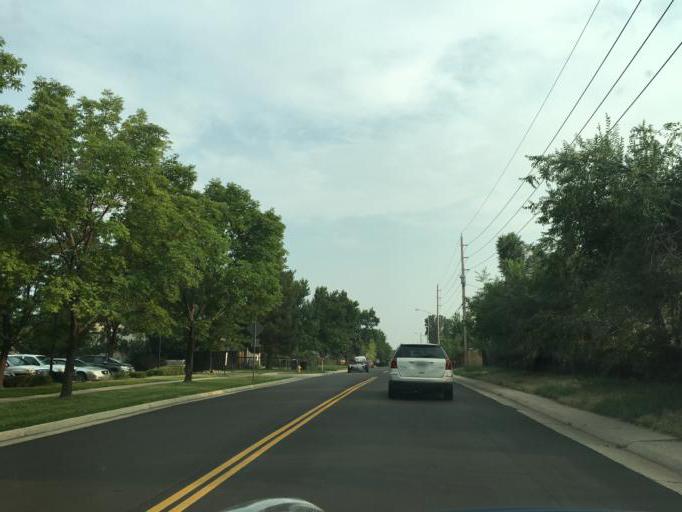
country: US
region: Colorado
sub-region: Arapahoe County
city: Glendale
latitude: 39.6890
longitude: -104.9318
